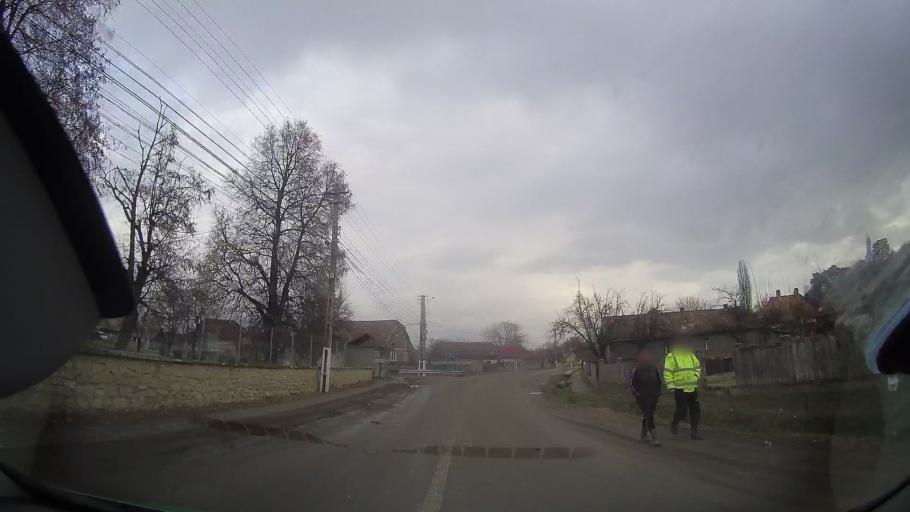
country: RO
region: Cluj
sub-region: Comuna Moldovenesti
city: Moldovenesti
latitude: 46.4985
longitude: 23.6756
